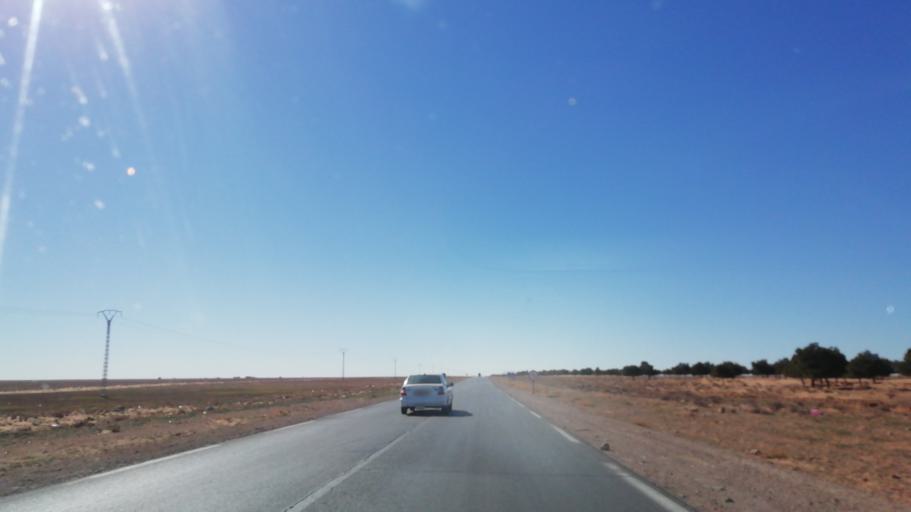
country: DZ
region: Saida
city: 'Ain el Hadjar
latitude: 33.9989
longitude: 0.0419
